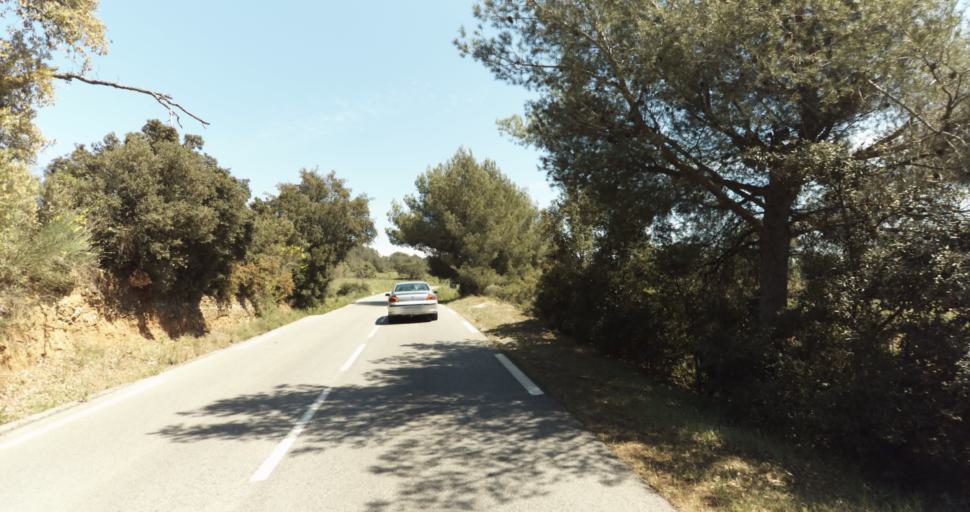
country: FR
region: Provence-Alpes-Cote d'Azur
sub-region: Departement du Var
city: Hyeres
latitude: 43.1514
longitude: 6.1448
